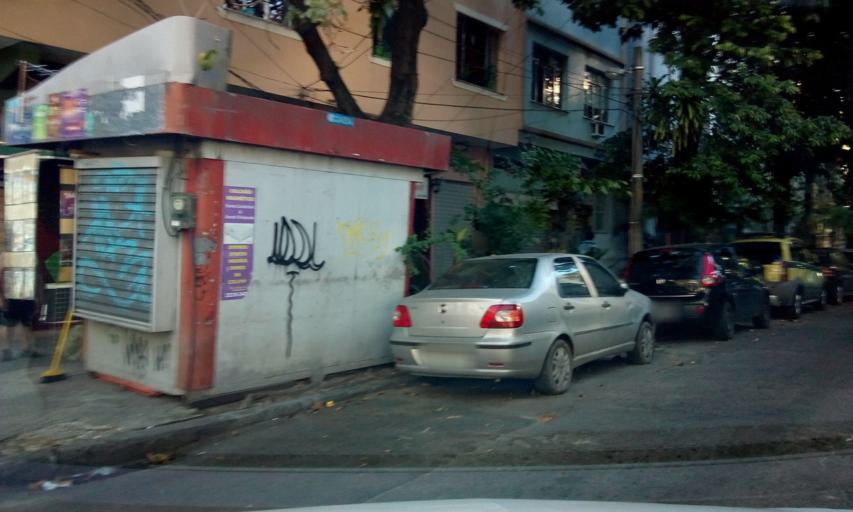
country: BR
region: Rio de Janeiro
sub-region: Rio De Janeiro
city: Rio de Janeiro
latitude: -22.9552
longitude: -43.1833
